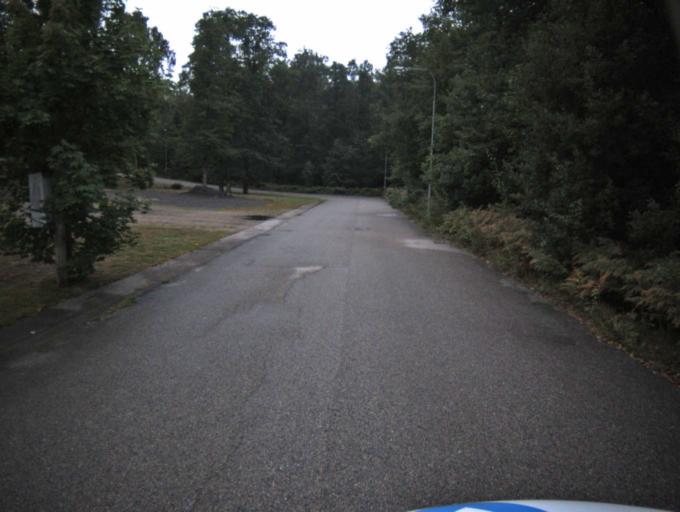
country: SE
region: Vaestra Goetaland
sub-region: Tranemo Kommun
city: Limmared
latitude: 57.6218
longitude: 13.4629
